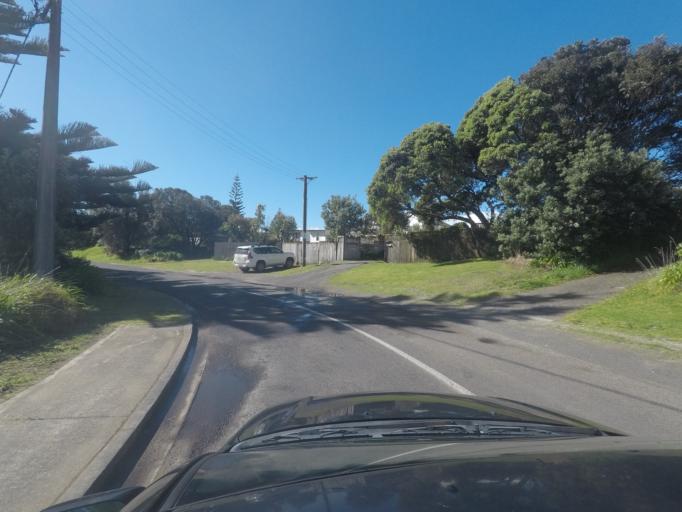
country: NZ
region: Bay of Plenty
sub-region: Western Bay of Plenty District
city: Waihi Beach
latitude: -37.4113
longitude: 175.9462
